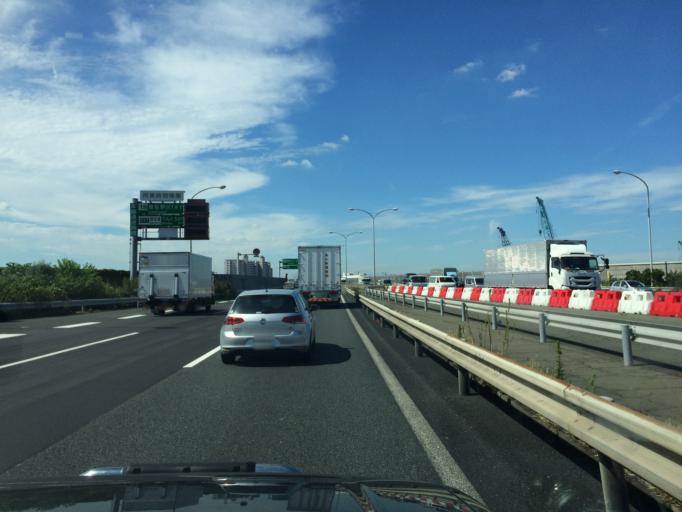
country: JP
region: Osaka
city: Matsubara
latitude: 34.5285
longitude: 135.5123
